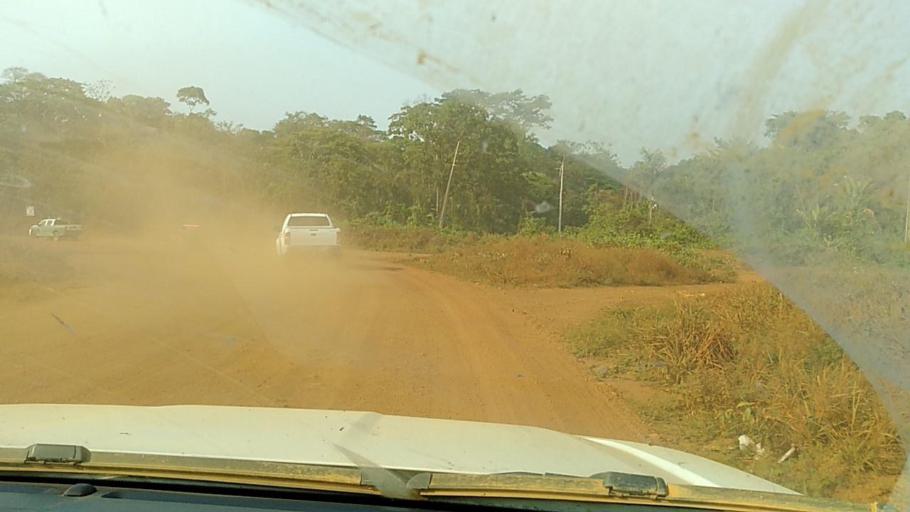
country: BR
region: Rondonia
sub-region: Porto Velho
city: Porto Velho
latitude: -8.7387
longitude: -63.9684
